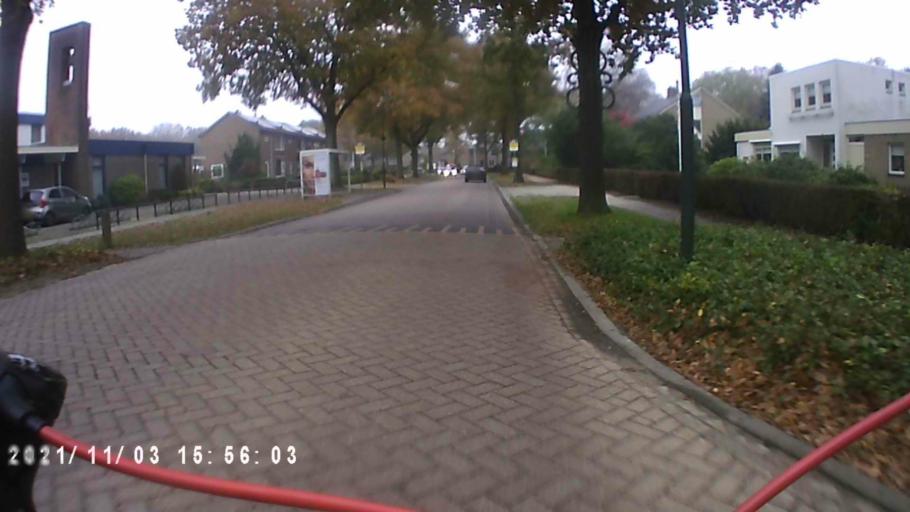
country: NL
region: Groningen
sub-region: Gemeente Leek
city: Leek
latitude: 53.0632
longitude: 6.3310
